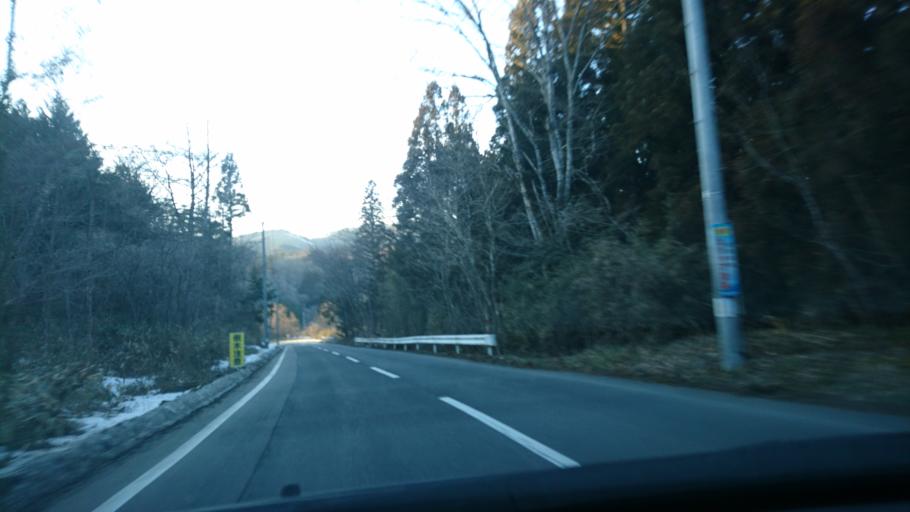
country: JP
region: Iwate
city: Mizusawa
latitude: 39.0458
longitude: 141.3354
